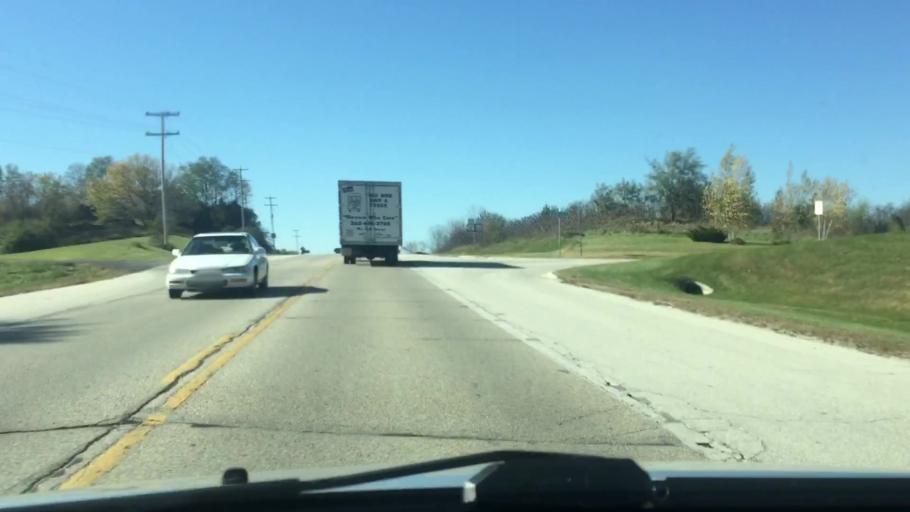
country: US
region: Wisconsin
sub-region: Waukesha County
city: Waukesha
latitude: 42.9883
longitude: -88.3007
